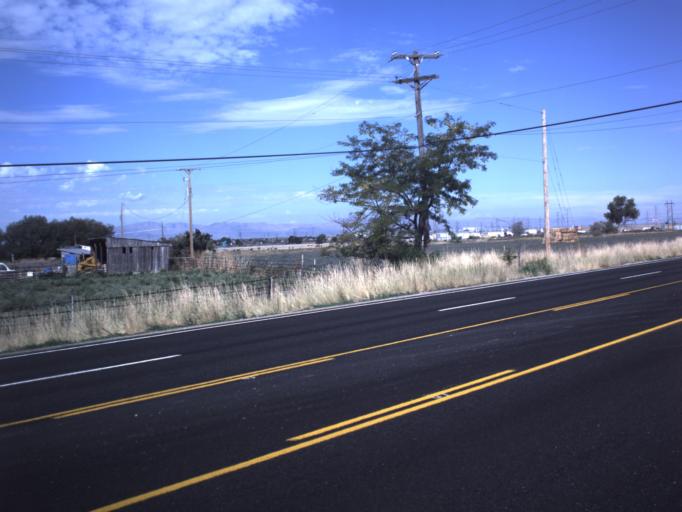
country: US
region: Utah
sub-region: Weber County
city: Pleasant View
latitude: 41.3285
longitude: -112.0221
